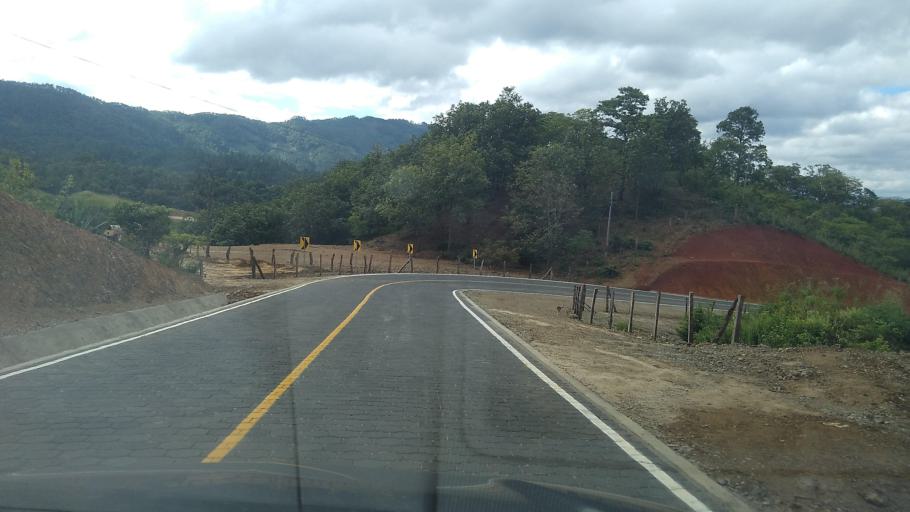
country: HN
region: El Paraiso
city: Santa Cruz
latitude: 13.7430
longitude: -86.6673
